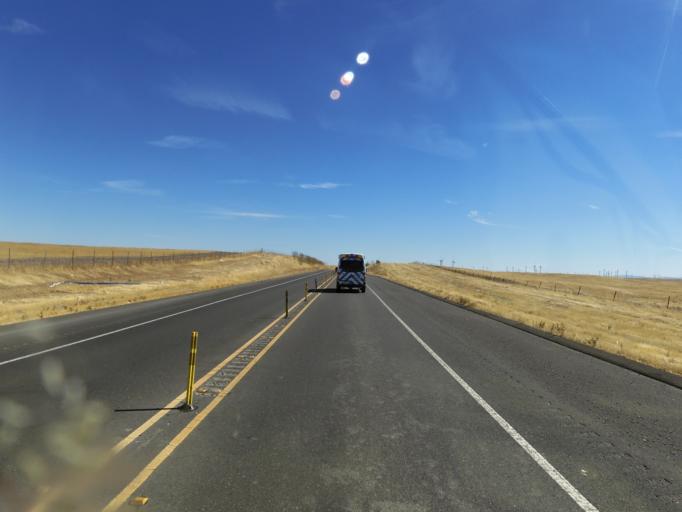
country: US
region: California
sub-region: Solano County
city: Suisun
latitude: 38.2178
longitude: -121.8865
